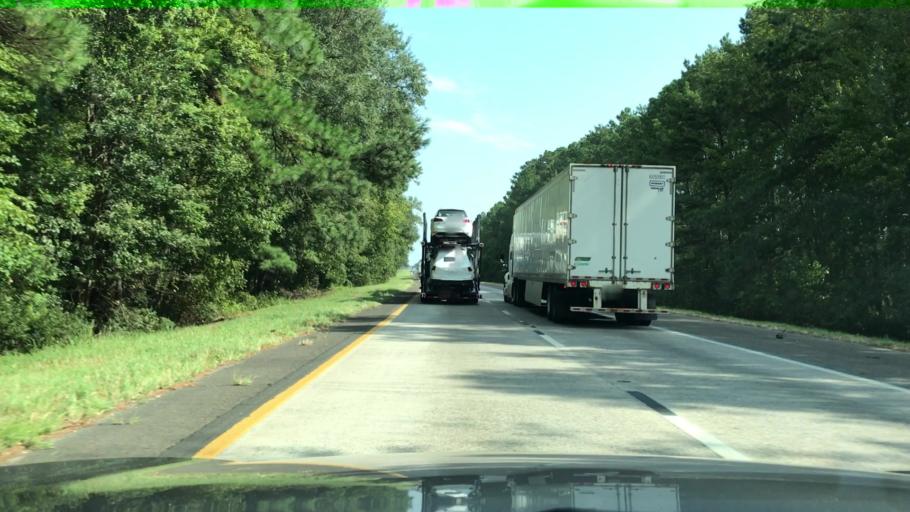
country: US
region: South Carolina
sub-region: Colleton County
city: Walterboro
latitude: 32.8267
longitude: -80.7485
